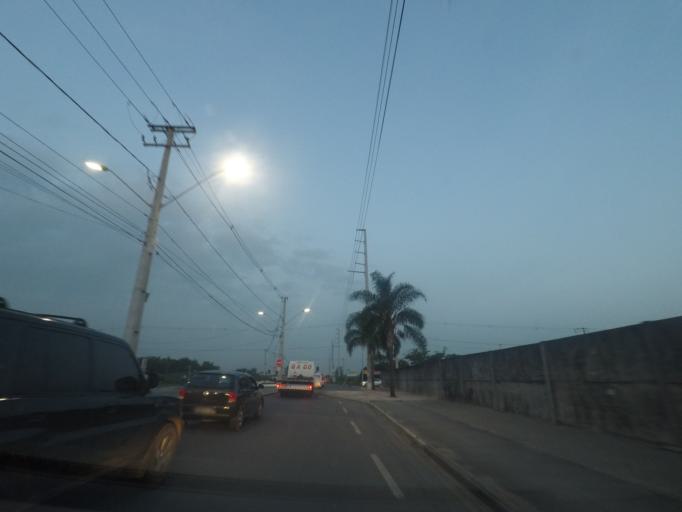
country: BR
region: Parana
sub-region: Pinhais
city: Pinhais
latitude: -25.4540
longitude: -49.1721
